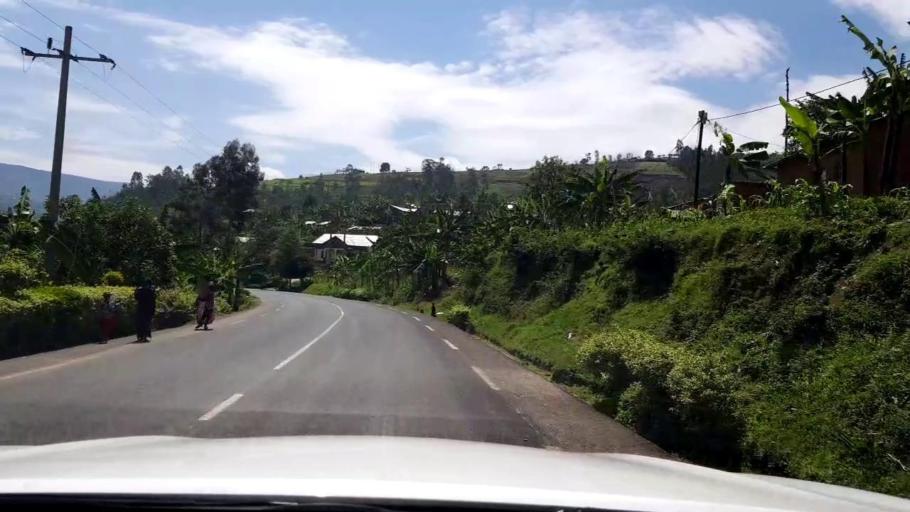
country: RW
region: Southern Province
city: Gitarama
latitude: -1.9200
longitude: 29.6473
